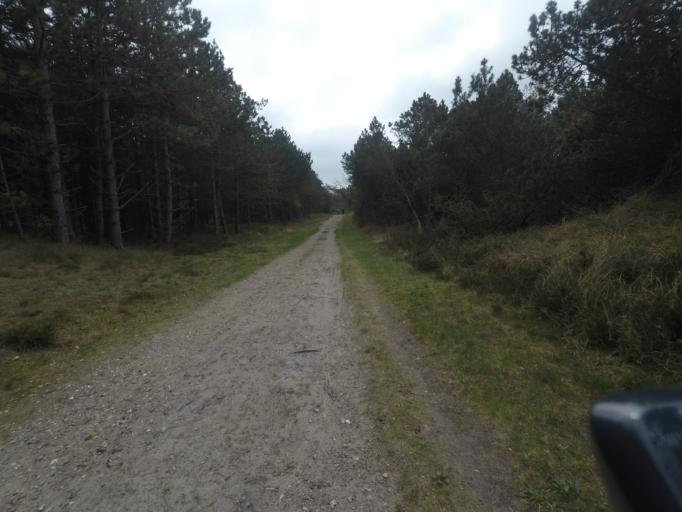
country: DE
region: Schleswig-Holstein
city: List
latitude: 55.0978
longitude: 8.5243
